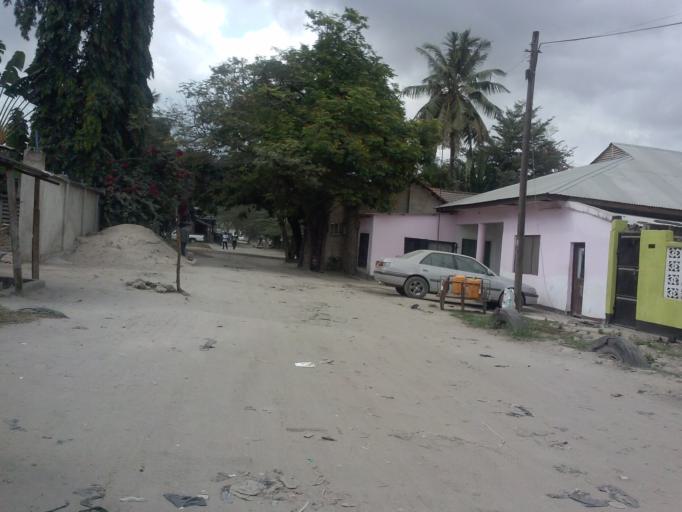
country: TZ
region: Dar es Salaam
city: Magomeni
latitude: -6.7765
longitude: 39.2405
